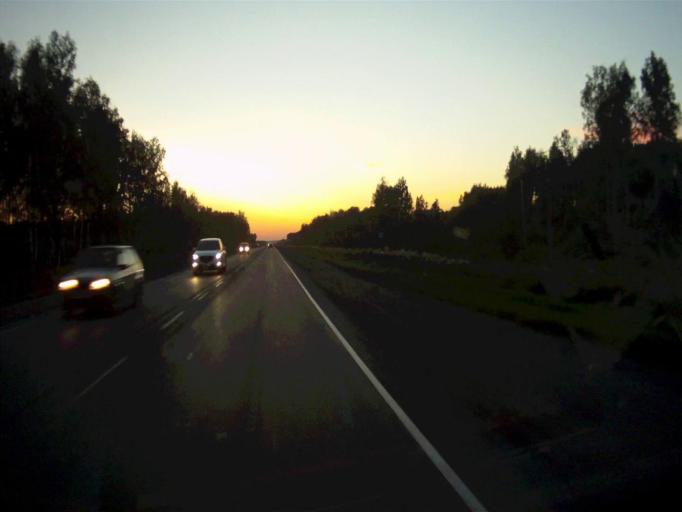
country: RU
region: Chelyabinsk
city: Poletayevo
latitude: 55.2104
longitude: 61.0824
